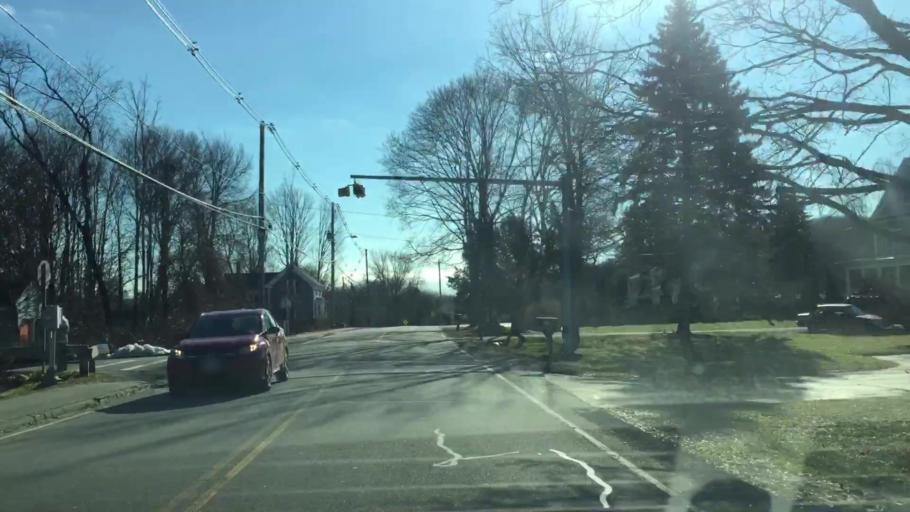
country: US
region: Massachusetts
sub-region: Essex County
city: Andover
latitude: 42.6690
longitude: -71.1005
